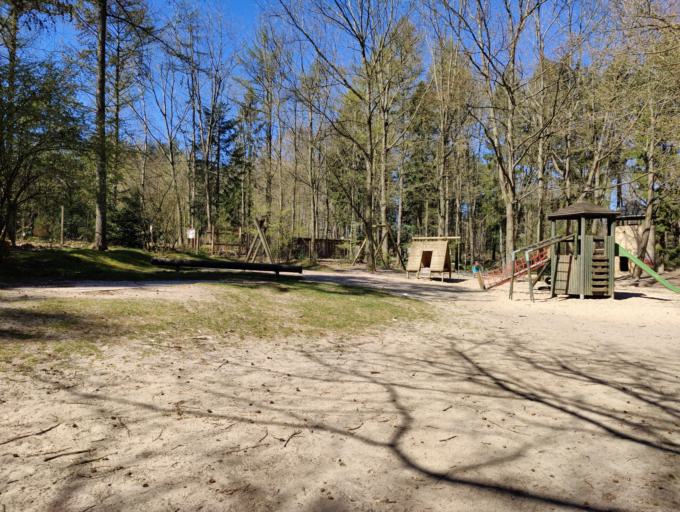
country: DE
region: Schleswig-Holstein
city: Burg
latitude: 54.0020
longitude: 9.2444
